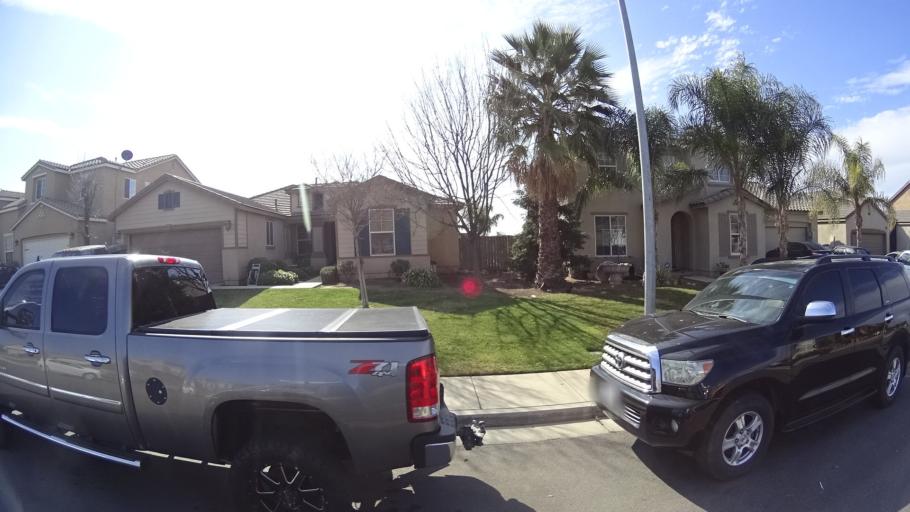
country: US
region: California
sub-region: Kern County
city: Lamont
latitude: 35.3908
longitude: -118.8849
